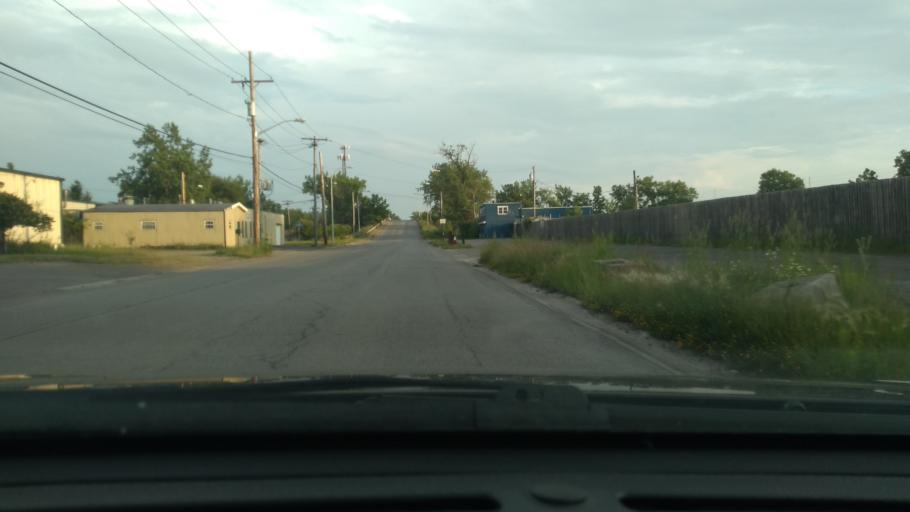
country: US
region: New York
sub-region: Erie County
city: Lackawanna
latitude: 42.8396
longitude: -78.8325
